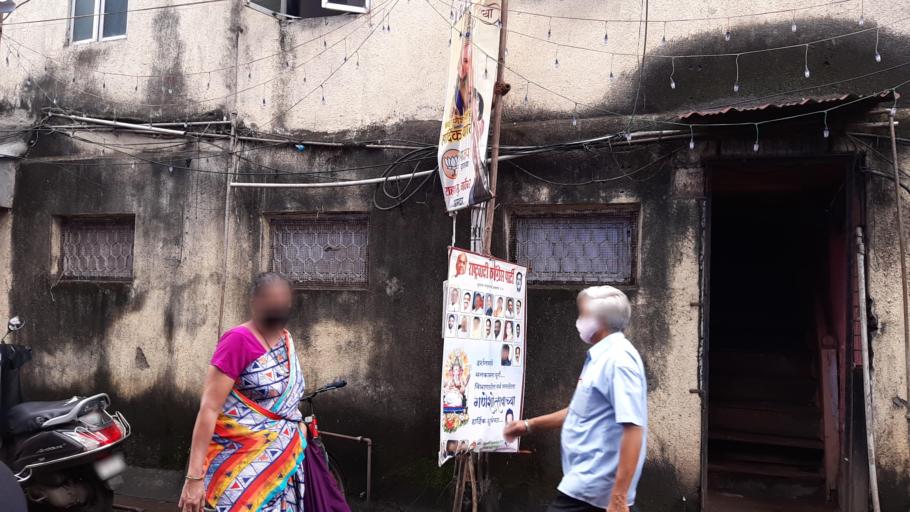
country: IN
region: Maharashtra
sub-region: Raigarh
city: Uran
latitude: 18.9478
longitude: 72.8261
